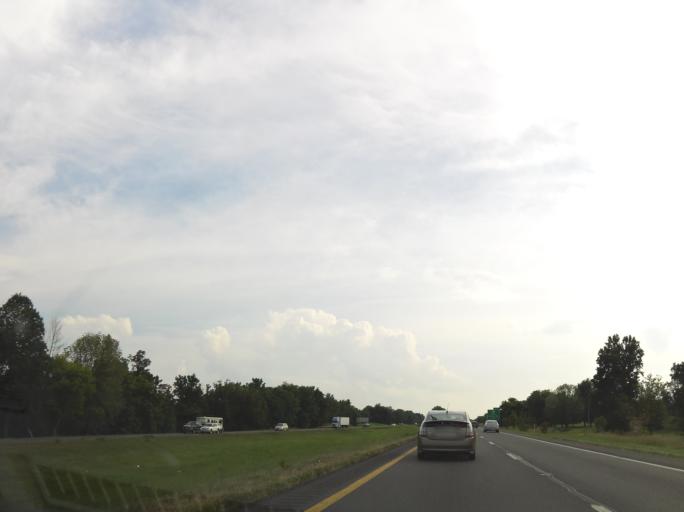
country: US
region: West Virginia
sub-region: Berkeley County
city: Martinsburg
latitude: 39.4222
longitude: -78.0051
